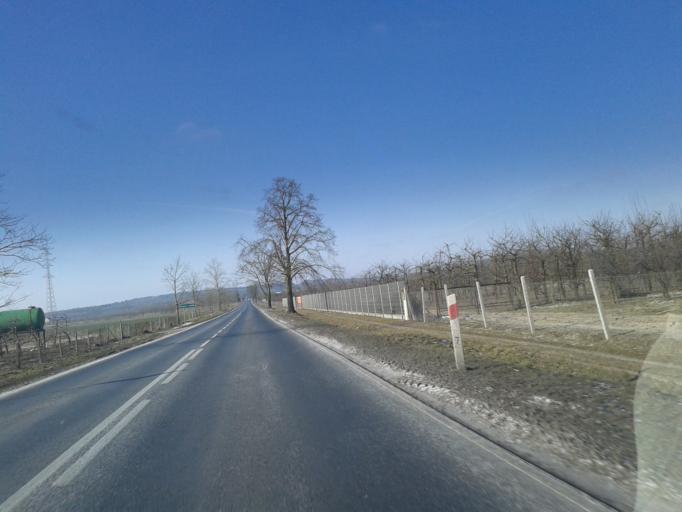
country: PL
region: Greater Poland Voivodeship
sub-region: Powiat pilski
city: Wysoka
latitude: 53.1407
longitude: 17.0867
